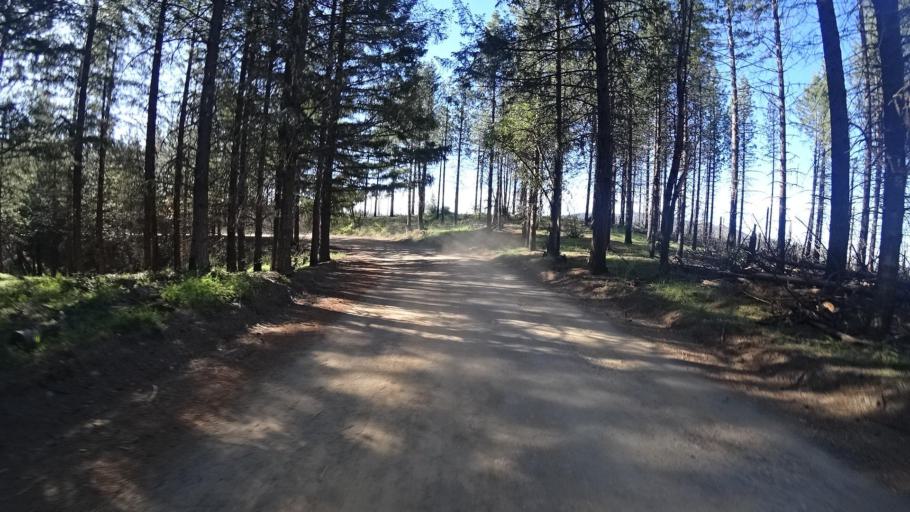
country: US
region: California
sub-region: Lake County
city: Upper Lake
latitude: 39.3499
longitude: -122.9741
